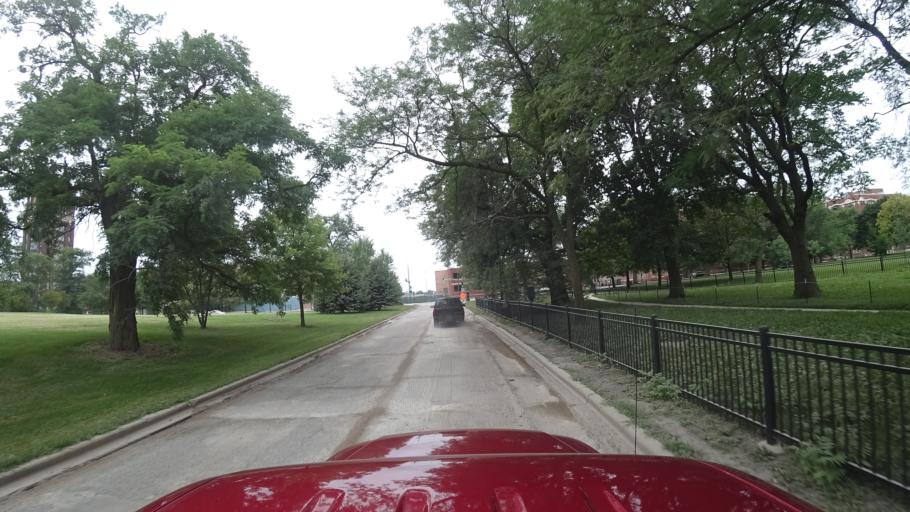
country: US
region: Illinois
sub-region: Cook County
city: Chicago
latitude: 41.8240
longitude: -87.6769
